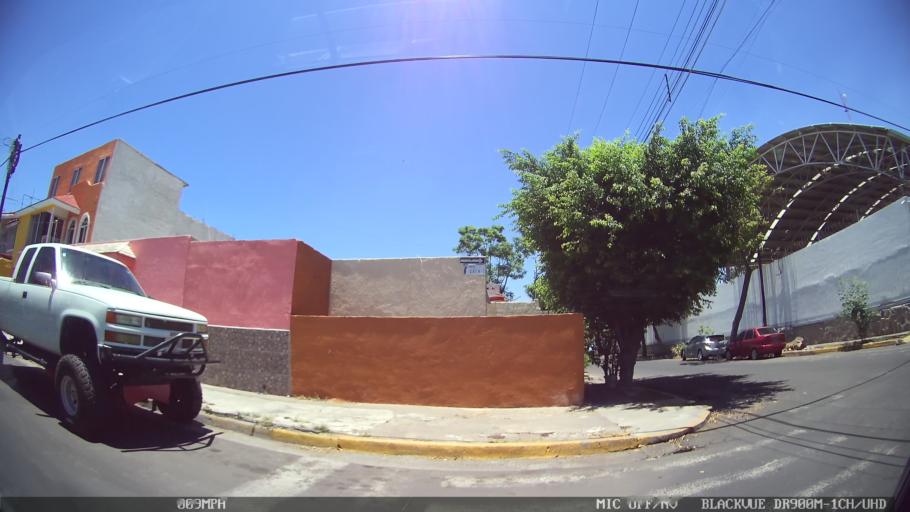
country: MX
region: Jalisco
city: Tlaquepaque
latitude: 20.6753
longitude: -103.2861
